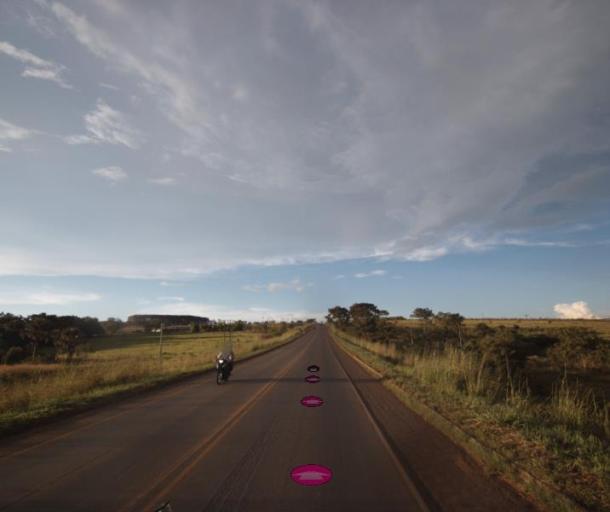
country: BR
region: Goias
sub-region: Anapolis
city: Anapolis
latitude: -16.2713
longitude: -48.9401
